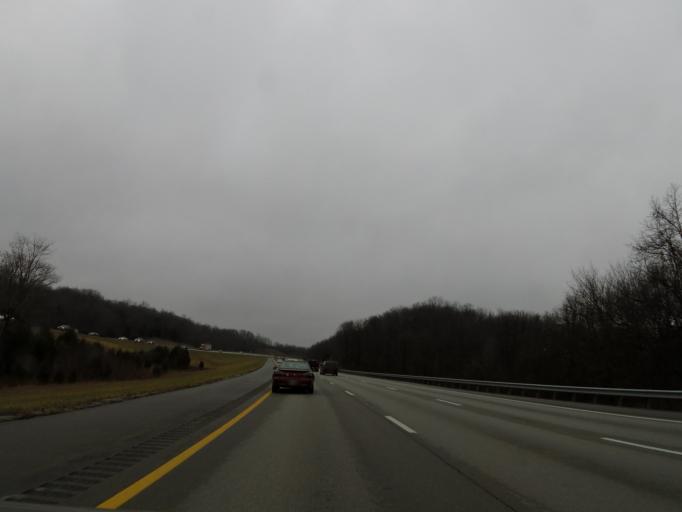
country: US
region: Kentucky
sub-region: Scott County
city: Georgetown
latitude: 38.3260
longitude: -84.5626
